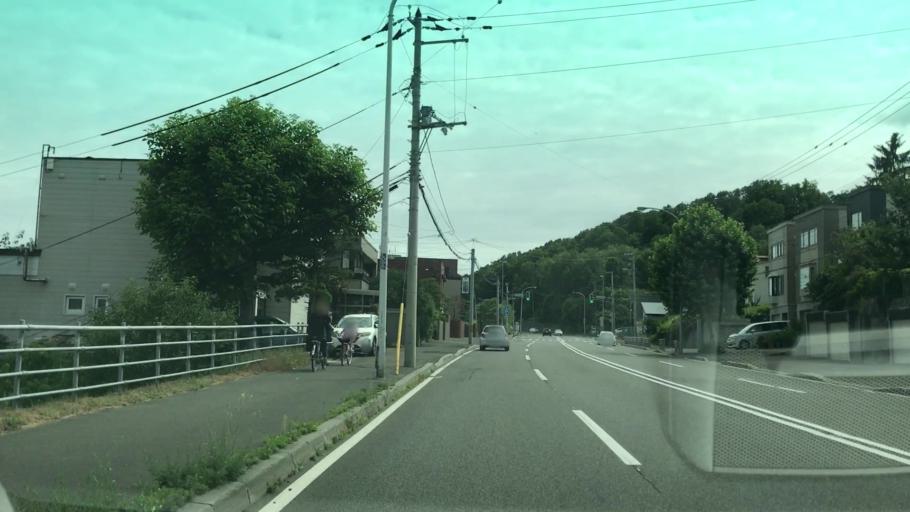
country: JP
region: Hokkaido
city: Sapporo
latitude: 42.9829
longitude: 141.3471
